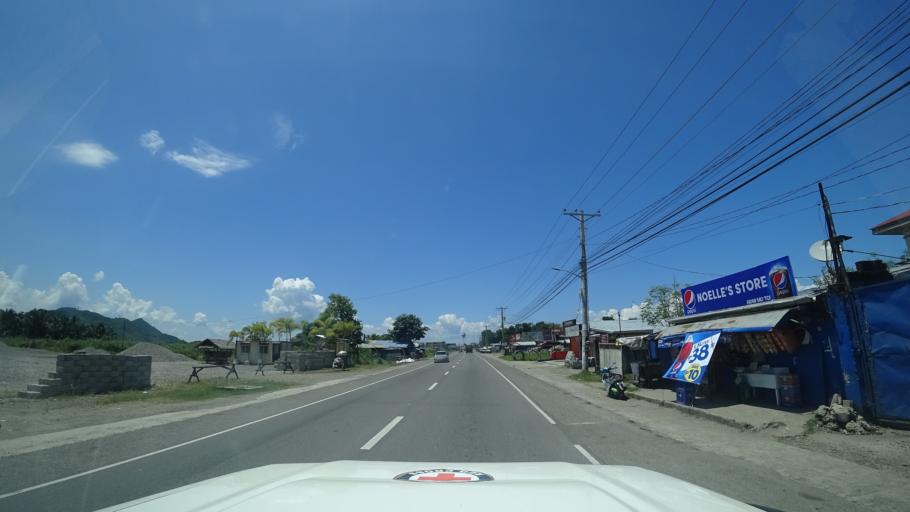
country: PH
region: Eastern Visayas
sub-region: Province of Leyte
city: Pawing
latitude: 11.1733
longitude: 124.9997
